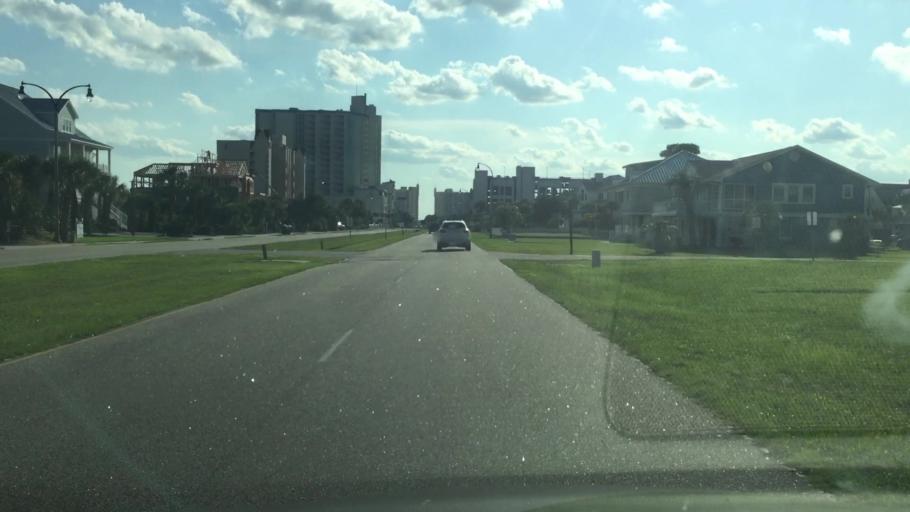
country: US
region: South Carolina
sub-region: Horry County
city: North Myrtle Beach
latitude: 33.8220
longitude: -78.6638
